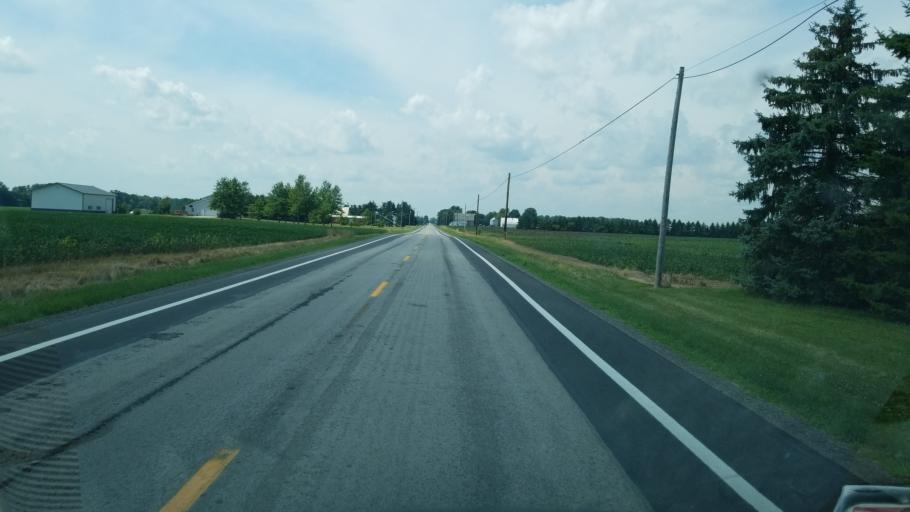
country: US
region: Ohio
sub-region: Hancock County
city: Arlington
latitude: 40.8925
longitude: -83.6878
